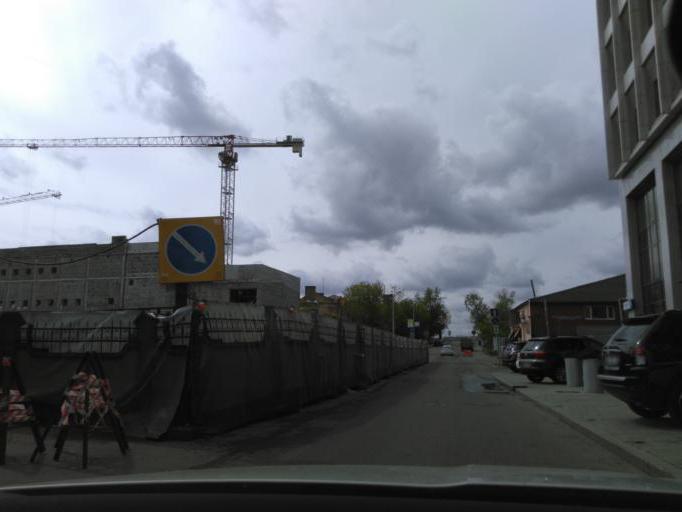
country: RU
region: Moscow
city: Zamoskvorech'ye
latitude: 55.7243
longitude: 37.6441
